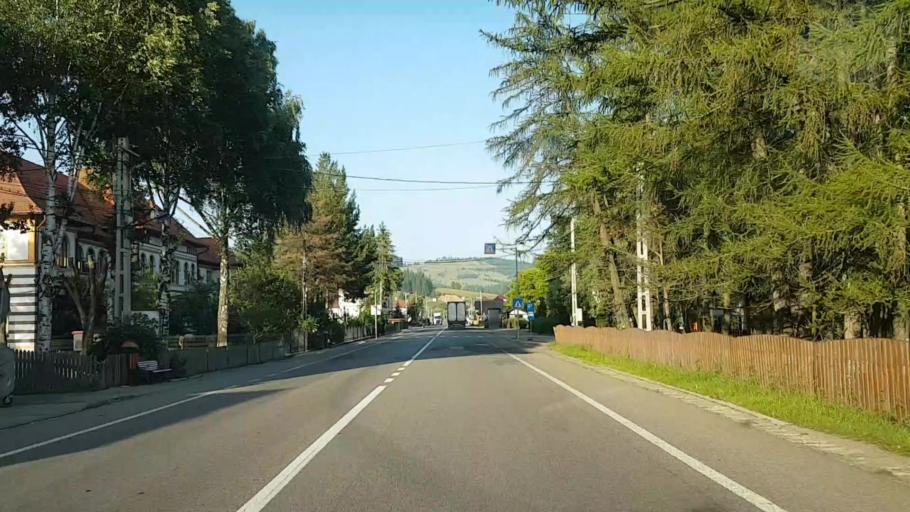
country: RO
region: Suceava
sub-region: Comuna Dorna Candrenilor
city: Dorna Candrenilor
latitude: 47.3550
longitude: 25.2633
